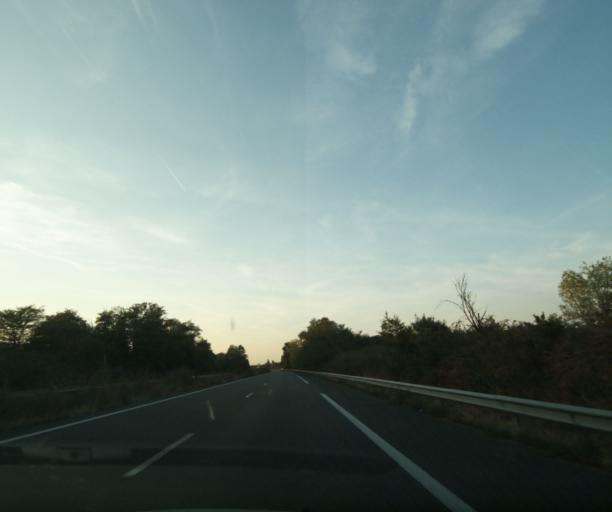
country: FR
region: Aquitaine
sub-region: Departement du Lot-et-Garonne
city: Tonneins
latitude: 44.3639
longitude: 0.2445
